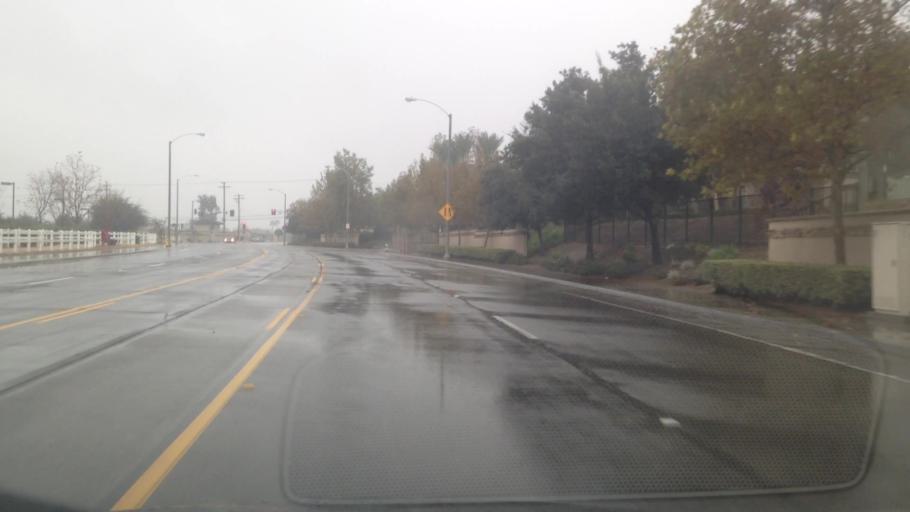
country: US
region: California
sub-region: Riverside County
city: Home Gardens
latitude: 33.9046
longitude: -117.4960
